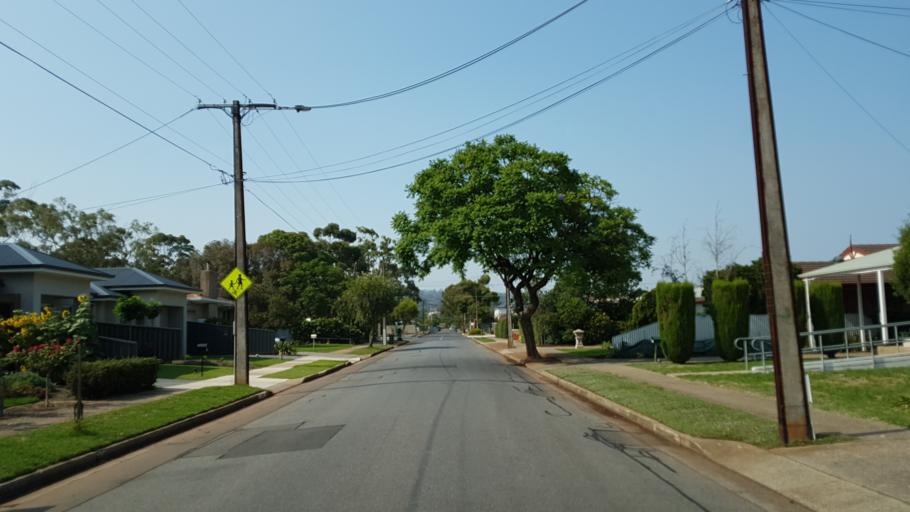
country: AU
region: South Australia
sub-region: Holdfast Bay
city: Seacliff Park
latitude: -35.0194
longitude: 138.5369
